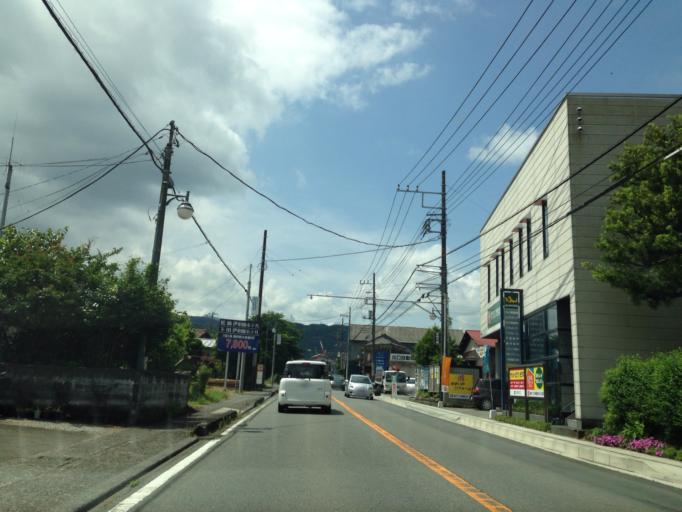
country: JP
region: Shizuoka
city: Heda
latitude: 34.9314
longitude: 138.9334
